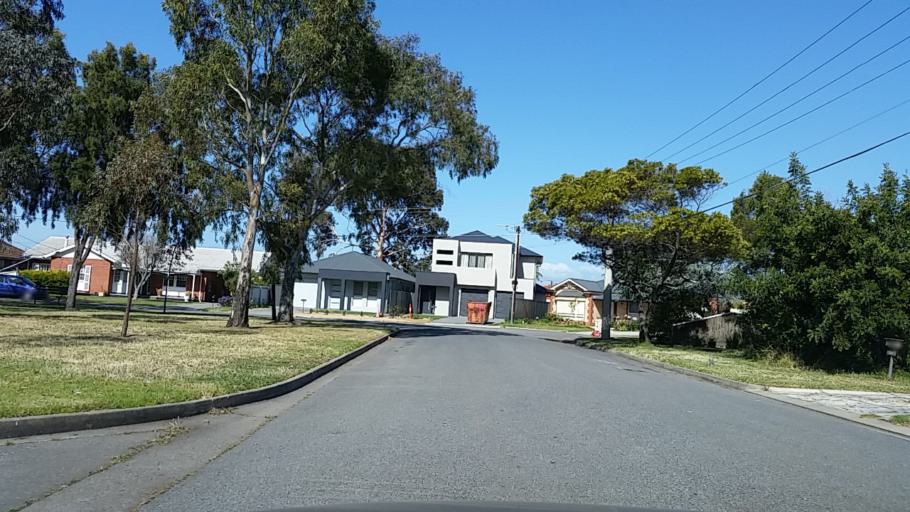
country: AU
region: South Australia
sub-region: Charles Sturt
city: Grange
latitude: -34.9111
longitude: 138.5029
